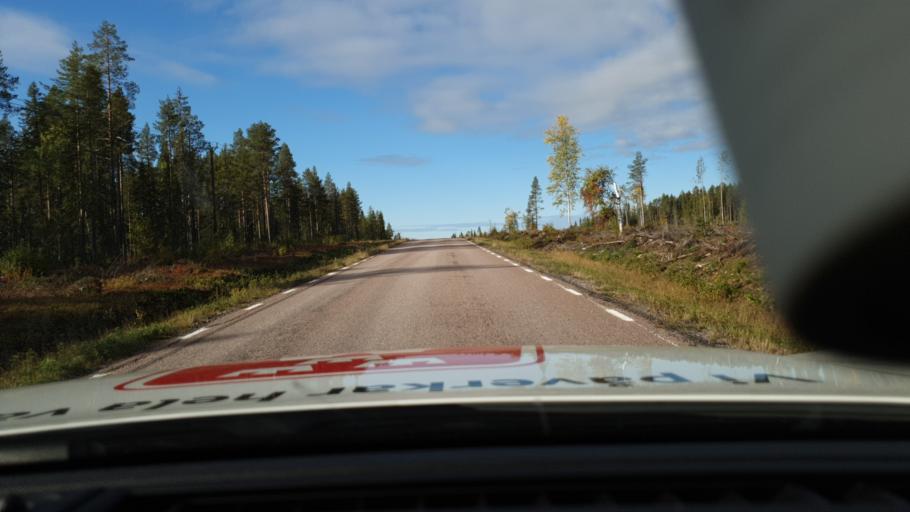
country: SE
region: Norrbotten
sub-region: Pajala Kommun
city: Pajala
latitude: 67.1906
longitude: 23.3075
